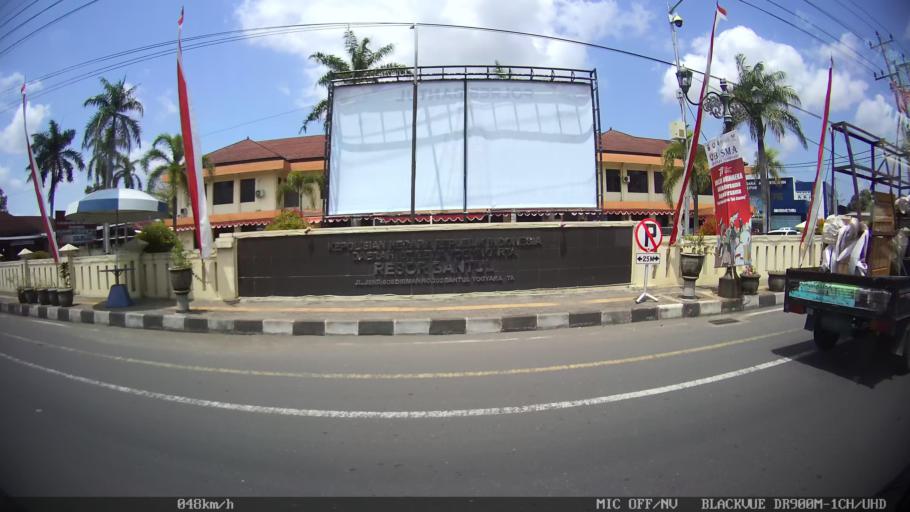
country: ID
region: Daerah Istimewa Yogyakarta
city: Bantul
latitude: -7.8894
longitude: 110.3270
